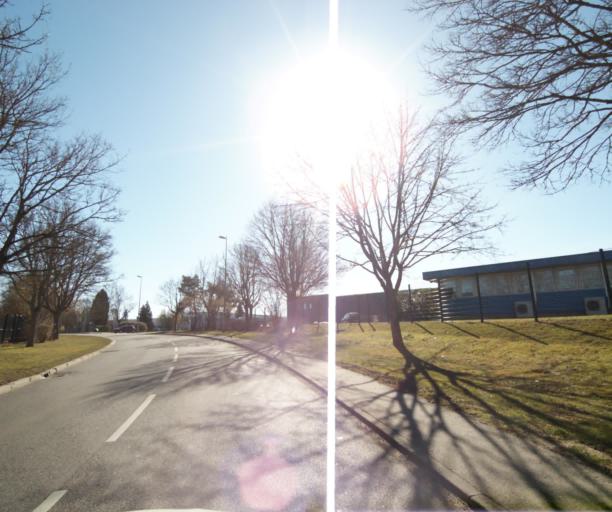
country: FR
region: Lorraine
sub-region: Departement de Meurthe-et-Moselle
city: Richardmenil
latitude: 48.6137
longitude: 6.1811
